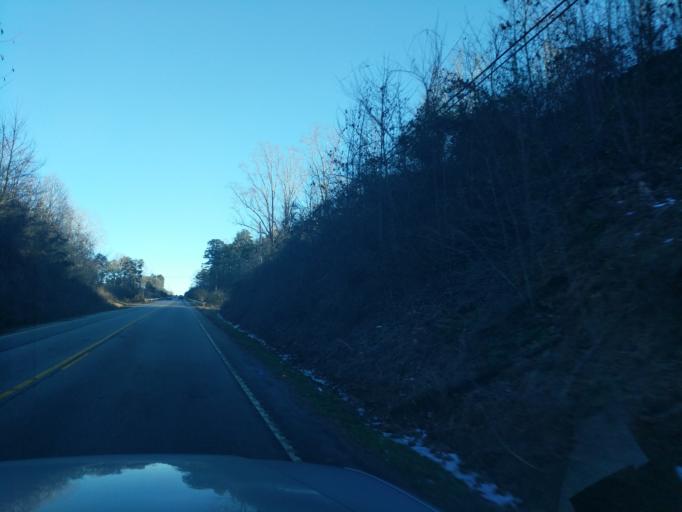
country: US
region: South Carolina
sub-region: Oconee County
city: Westminster
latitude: 34.6864
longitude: -83.1377
